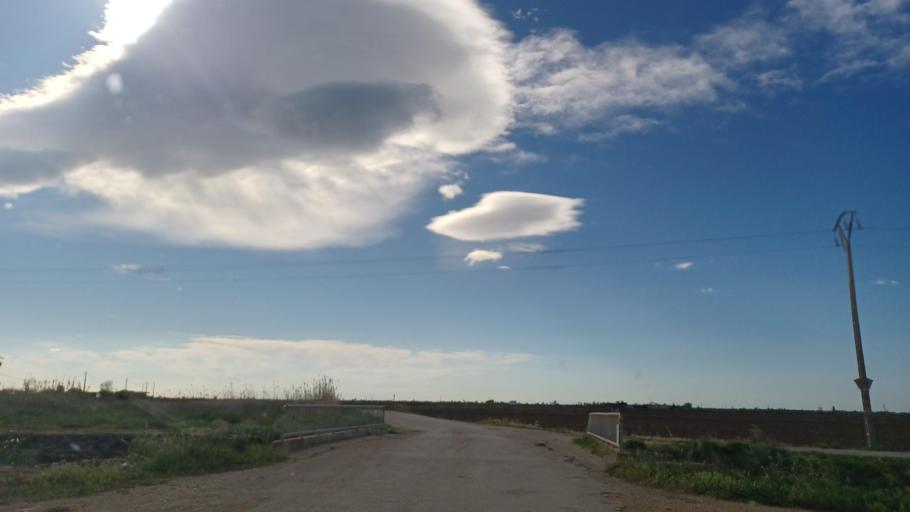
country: ES
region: Catalonia
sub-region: Provincia de Tarragona
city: L'Ampolla
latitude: 40.7700
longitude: 0.7012
